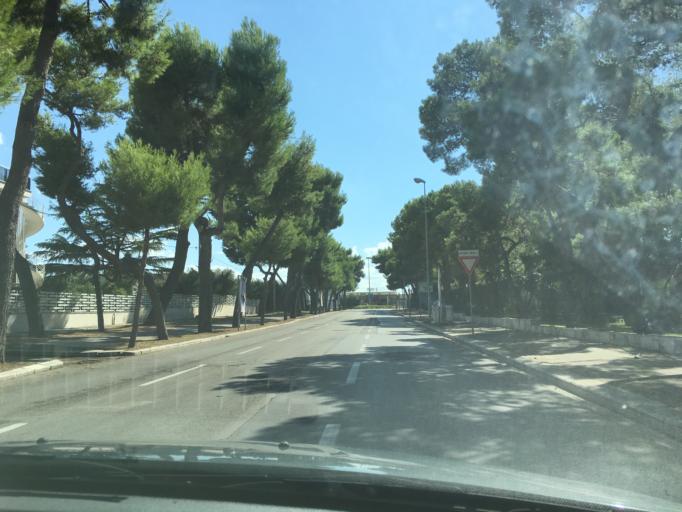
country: IT
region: Apulia
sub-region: Provincia di Bari
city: Bari
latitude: 41.1319
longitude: 16.8317
